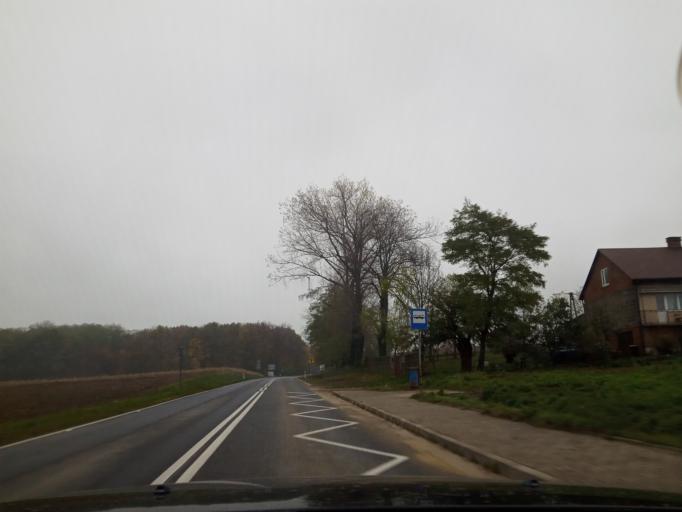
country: PL
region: Lesser Poland Voivodeship
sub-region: Powiat proszowicki
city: Klimontow
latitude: 50.2295
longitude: 20.3776
